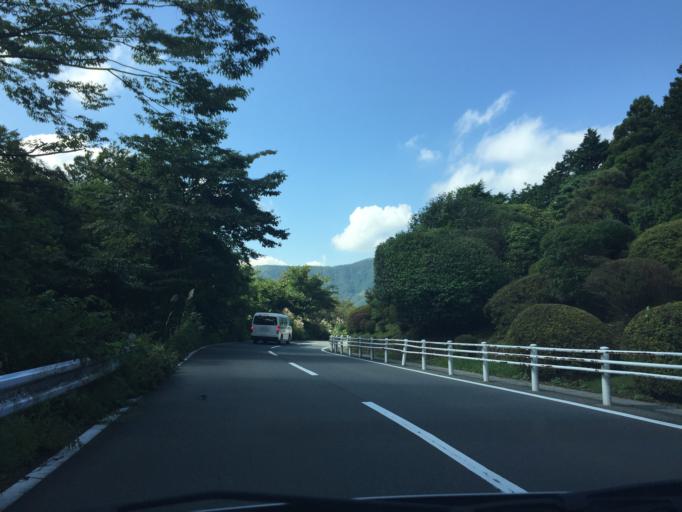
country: JP
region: Kanagawa
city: Hakone
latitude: 35.2456
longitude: 138.9982
